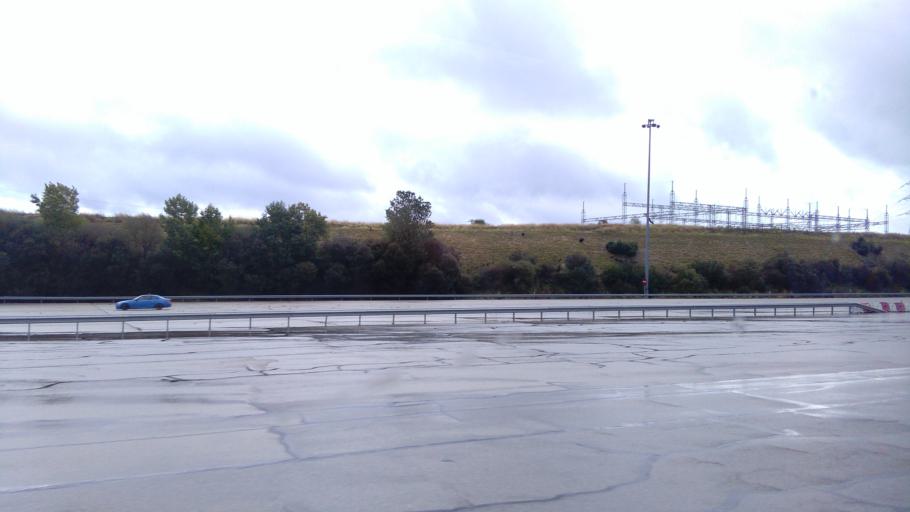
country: ES
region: Madrid
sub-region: Provincia de Madrid
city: Leganes
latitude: 40.3498
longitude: -3.7826
